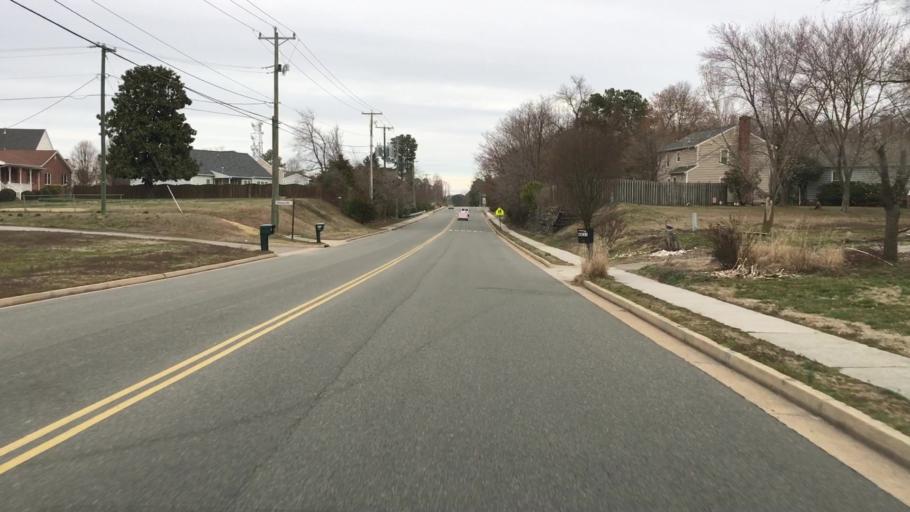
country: US
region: Virginia
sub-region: Henrico County
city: Laurel
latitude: 37.6561
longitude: -77.5459
